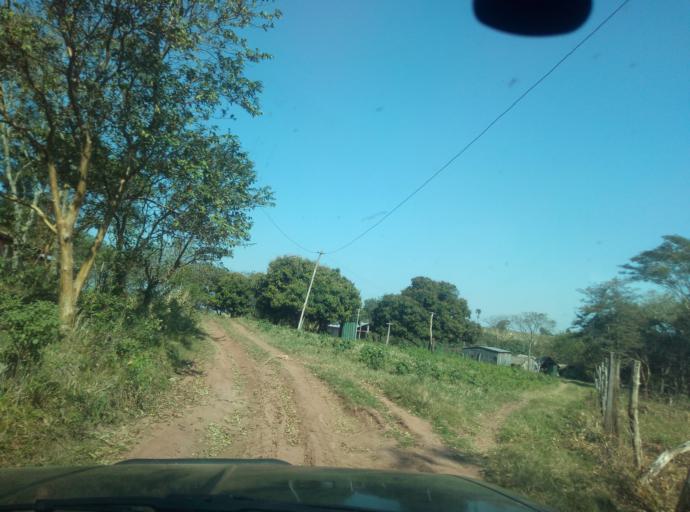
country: PY
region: Caaguazu
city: San Joaquin
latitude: -25.1735
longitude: -56.1124
